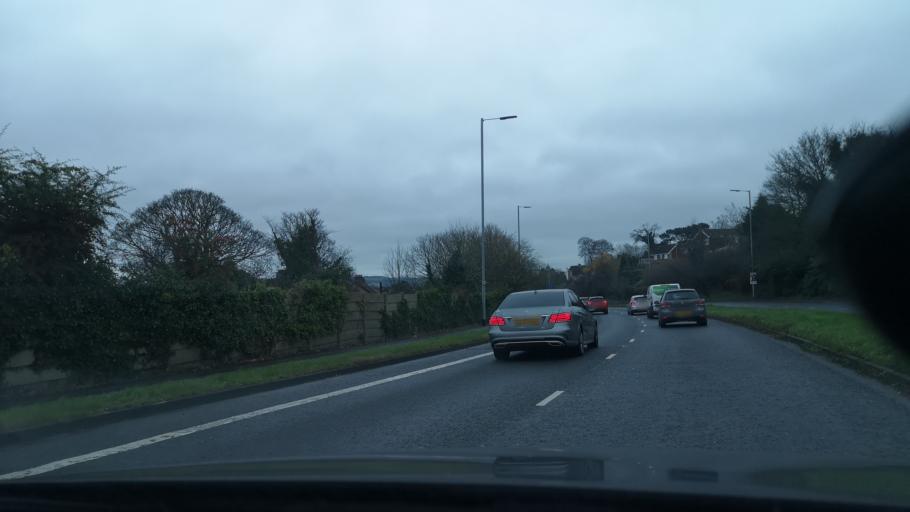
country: GB
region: Northern Ireland
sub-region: Castlereagh District
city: Castlereagh
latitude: 54.5703
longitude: -5.8897
